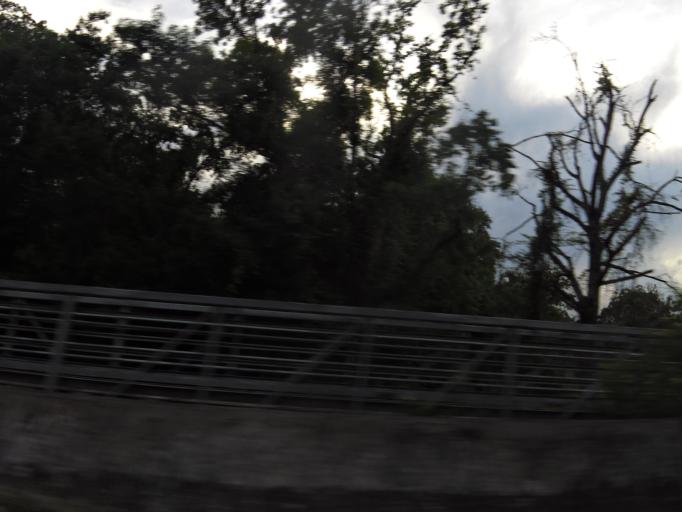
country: US
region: Florida
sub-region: Clay County
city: Bellair-Meadowbrook Terrace
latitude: 30.2951
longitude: -81.7983
